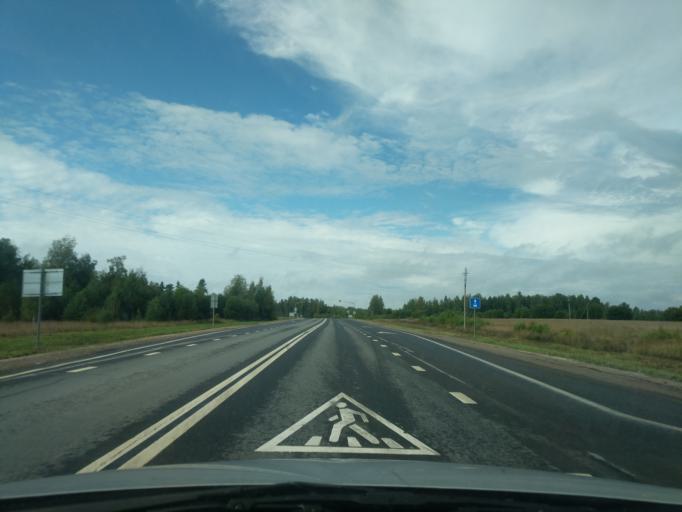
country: RU
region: Kostroma
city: Sudislavl'
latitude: 57.8302
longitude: 41.8857
